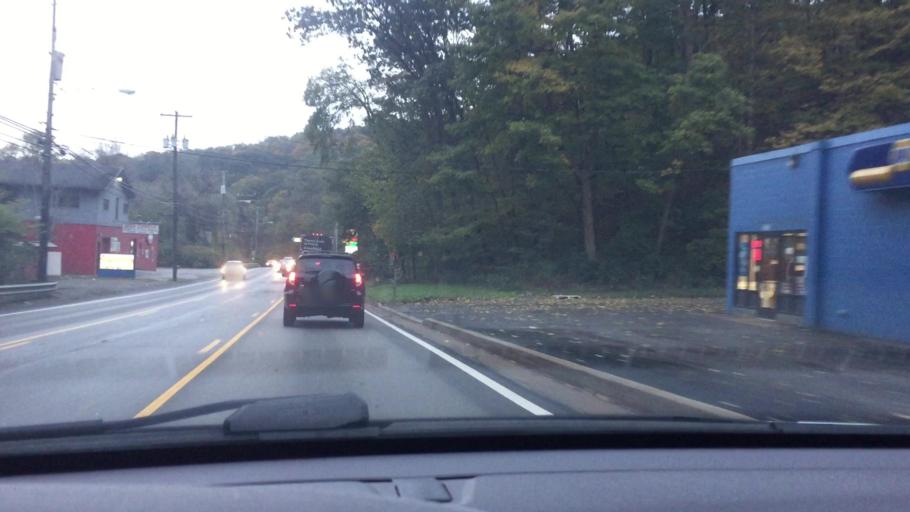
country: US
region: Pennsylvania
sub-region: Allegheny County
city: Ingram
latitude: 40.4412
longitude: -80.0940
